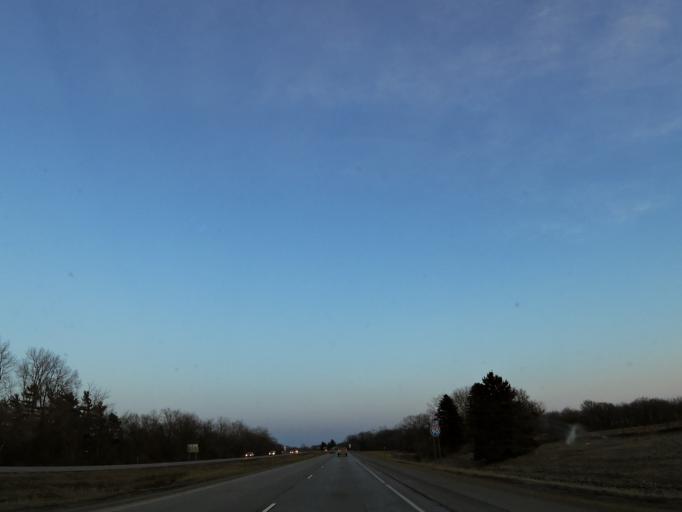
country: US
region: Minnesota
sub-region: Mower County
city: Austin
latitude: 43.6726
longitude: -92.9226
